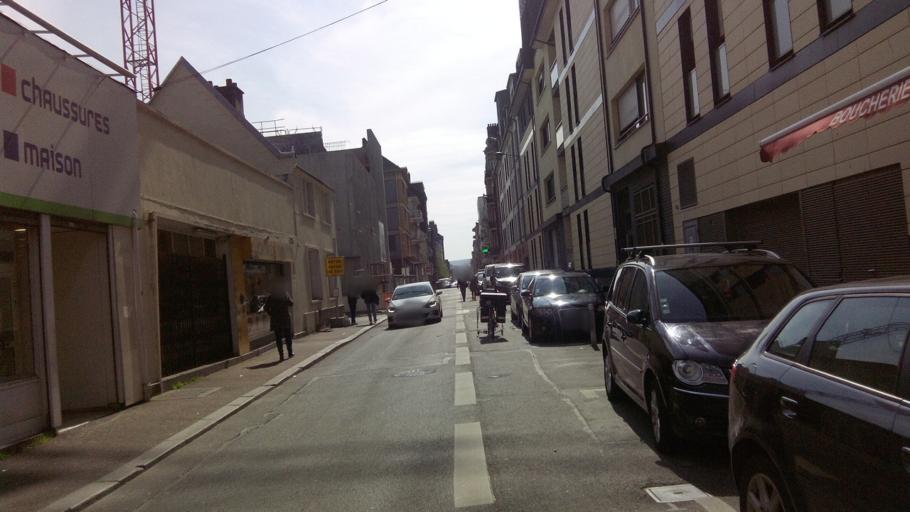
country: FR
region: Haute-Normandie
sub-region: Departement de la Seine-Maritime
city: Rouen
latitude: 49.4333
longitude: 1.0884
